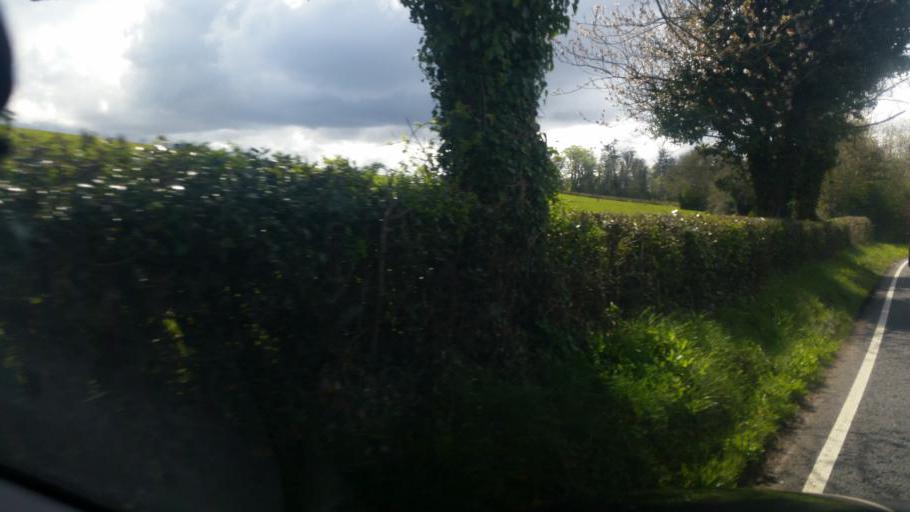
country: GB
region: Northern Ireland
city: Irvinestown
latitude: 54.4501
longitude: -7.8065
